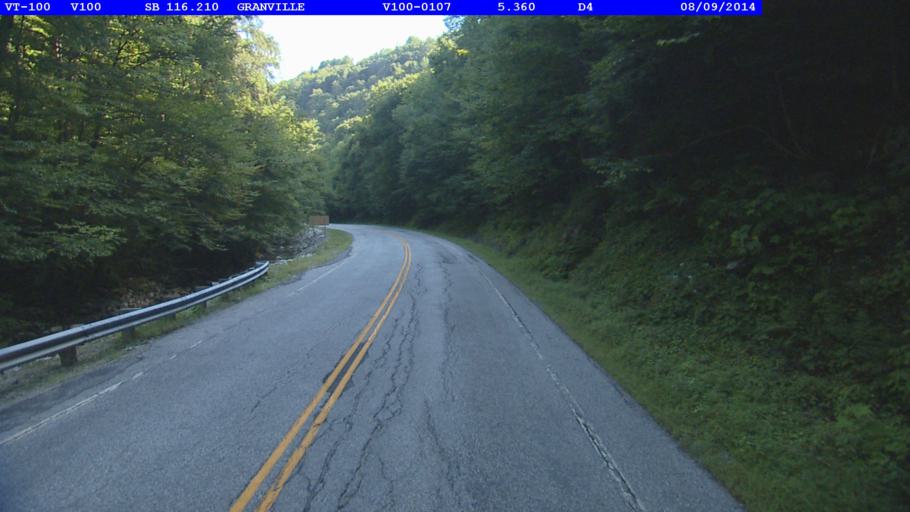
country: US
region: Vermont
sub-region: Orange County
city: Randolph
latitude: 44.0149
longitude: -72.8517
